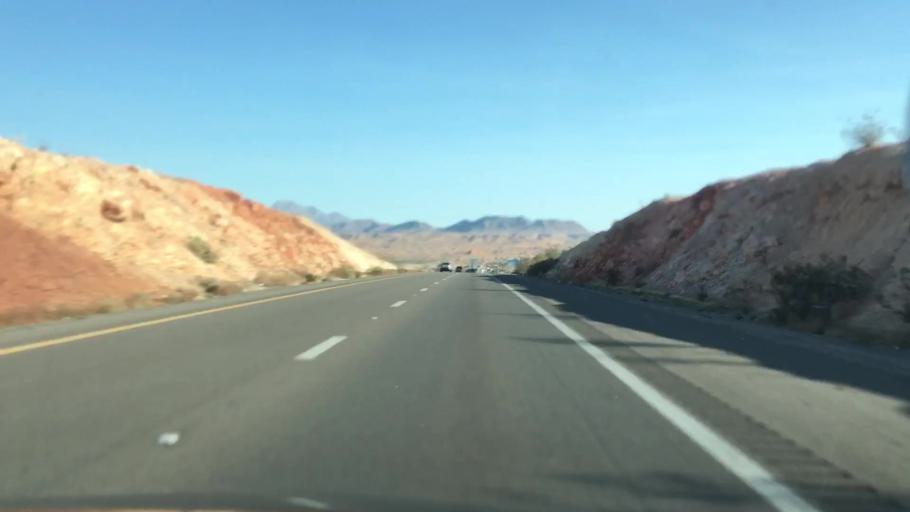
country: US
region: Nevada
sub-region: Clark County
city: Moapa Town
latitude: 36.6492
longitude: -114.5861
